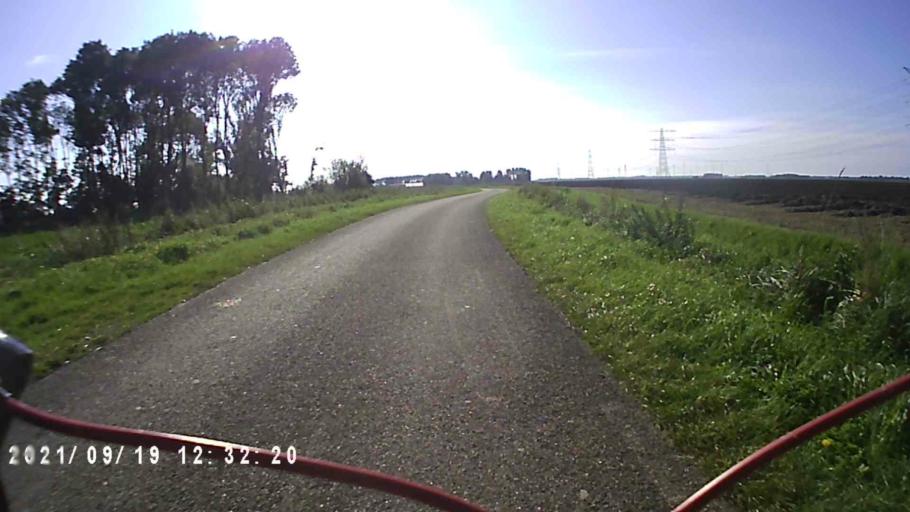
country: NL
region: Groningen
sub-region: Gemeente Slochteren
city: Slochteren
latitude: 53.2213
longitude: 6.9022
